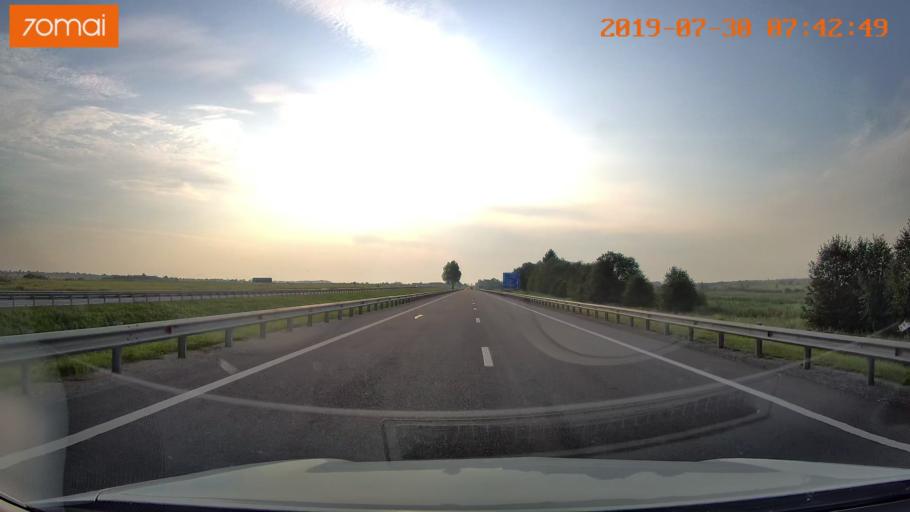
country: RU
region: Kaliningrad
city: Gvardeysk
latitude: 54.6482
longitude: 21.2896
